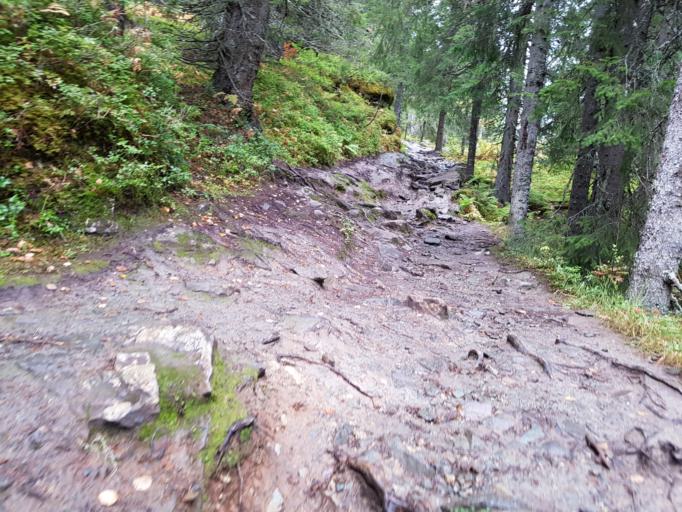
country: NO
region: Sor-Trondelag
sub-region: Melhus
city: Melhus
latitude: 63.4148
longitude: 10.2273
